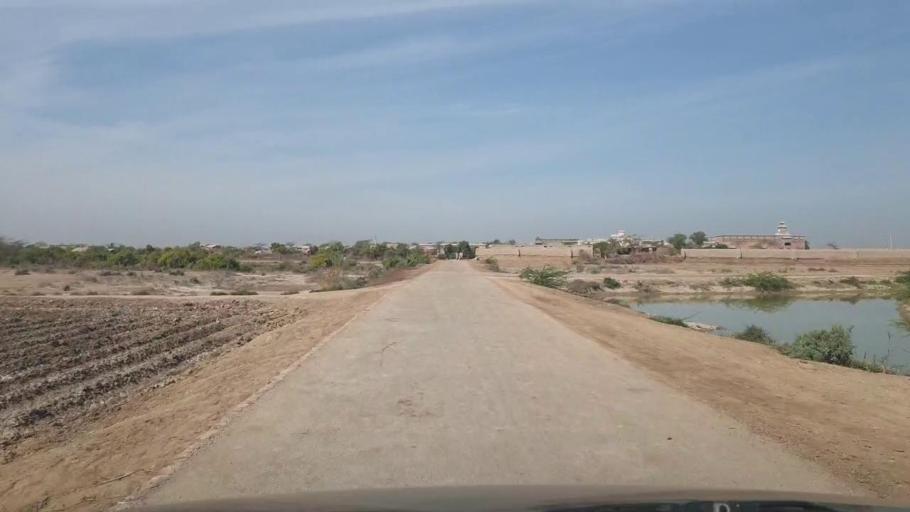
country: PK
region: Sindh
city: Umarkot
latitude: 25.3527
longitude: 69.5922
